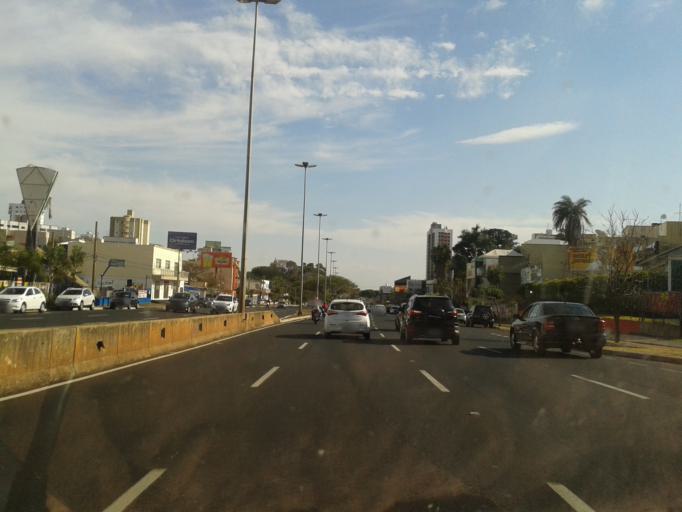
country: BR
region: Minas Gerais
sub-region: Uberlandia
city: Uberlandia
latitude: -18.9191
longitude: -48.2670
